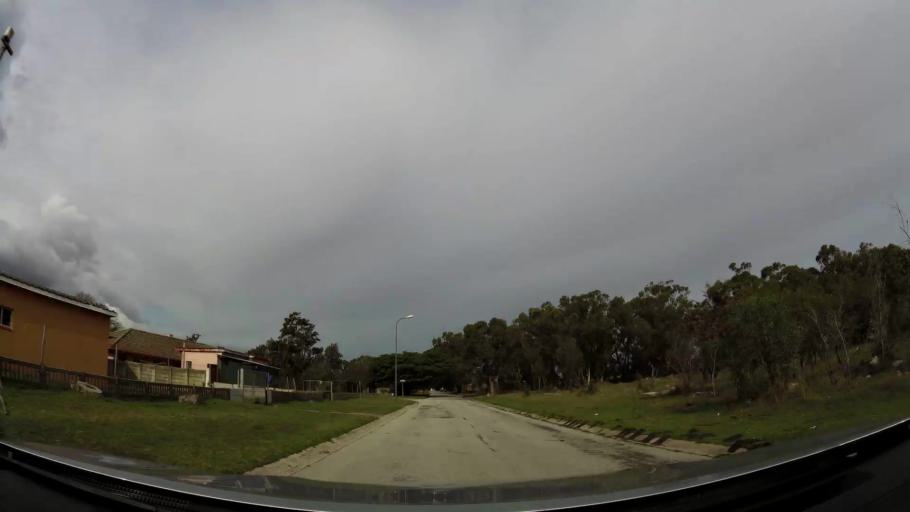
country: ZA
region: Eastern Cape
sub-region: Nelson Mandela Bay Metropolitan Municipality
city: Port Elizabeth
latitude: -33.9351
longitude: 25.4914
